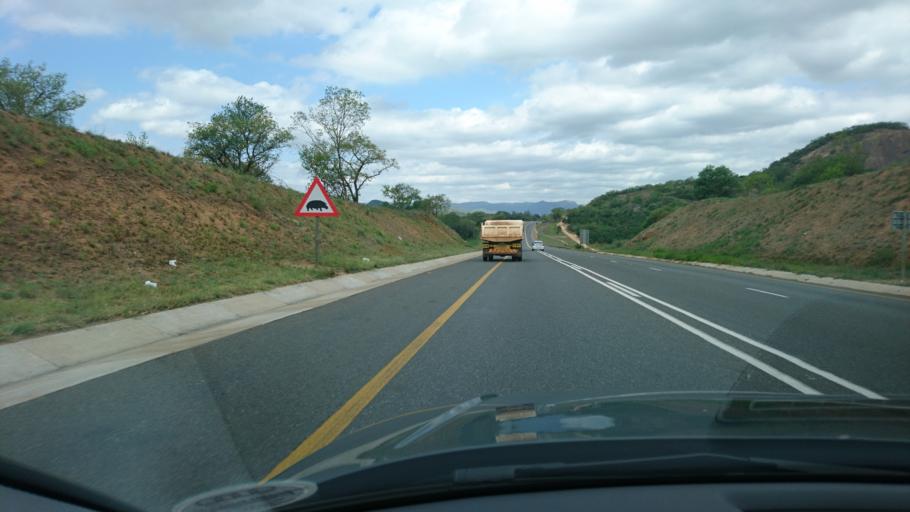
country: ZA
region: Mpumalanga
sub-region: Ehlanzeni District
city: Nelspruit
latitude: -25.4628
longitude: 31.0571
